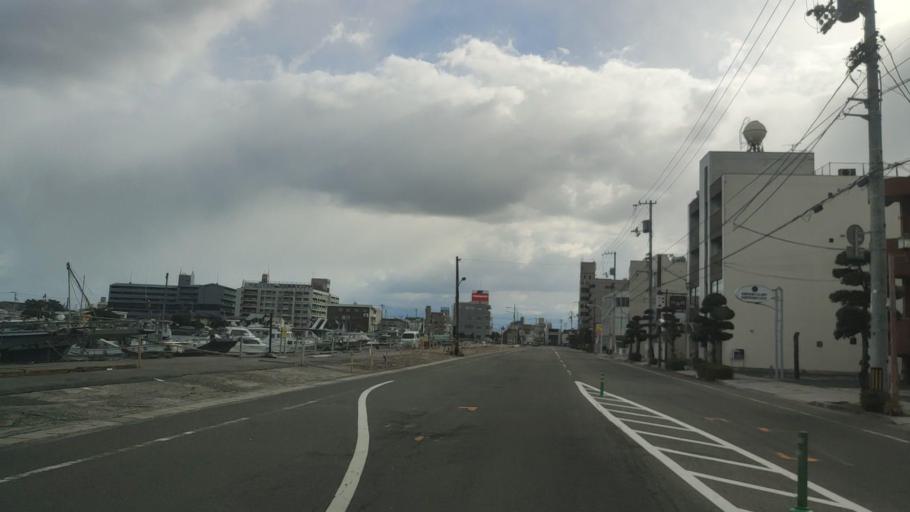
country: JP
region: Ehime
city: Saijo
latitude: 34.0678
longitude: 133.0052
